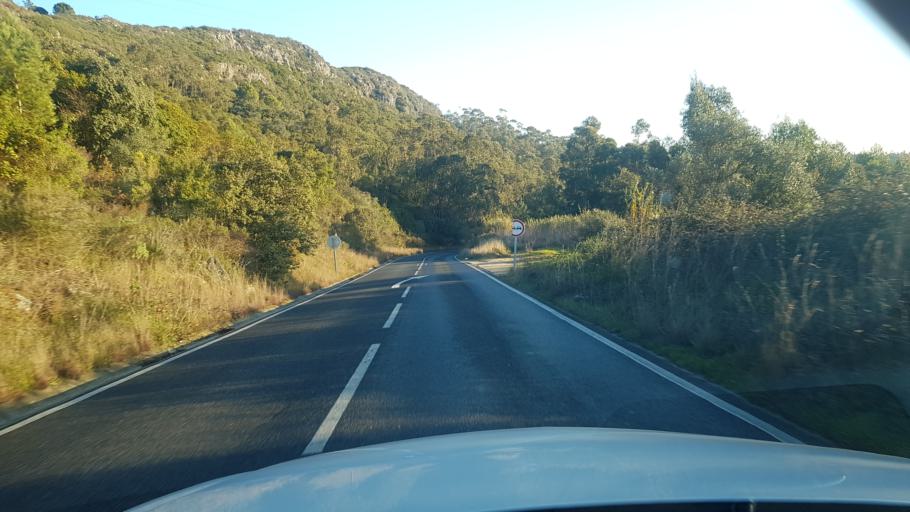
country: PT
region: Santarem
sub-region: Ourem
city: Ourem
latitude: 39.5585
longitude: -8.5772
